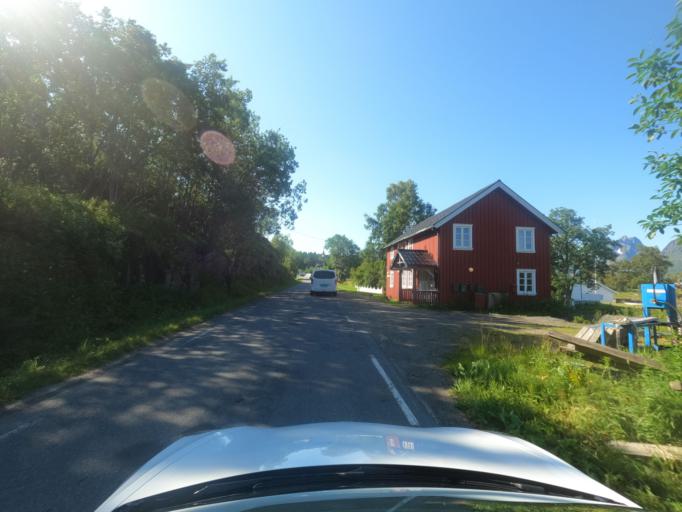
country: NO
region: Nordland
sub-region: Hadsel
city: Stokmarknes
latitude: 68.3145
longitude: 14.9891
